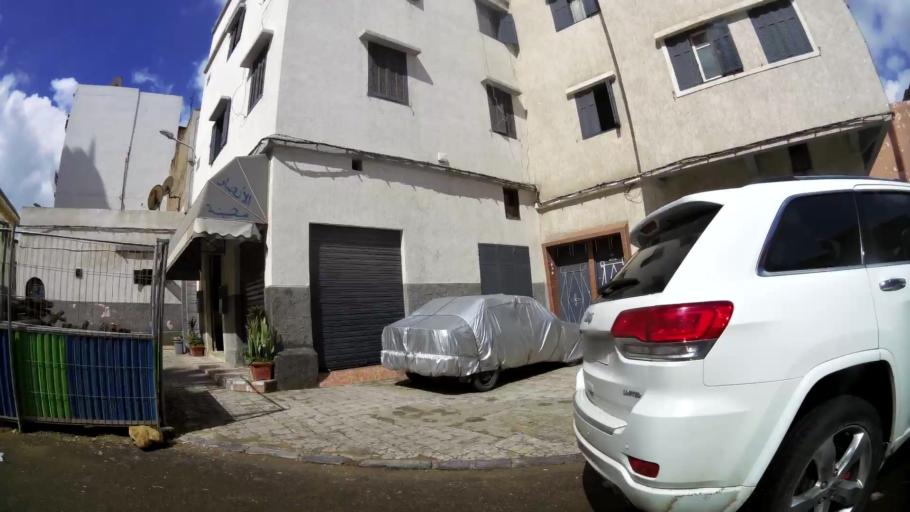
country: MA
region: Grand Casablanca
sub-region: Casablanca
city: Casablanca
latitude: 33.5493
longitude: -7.5978
